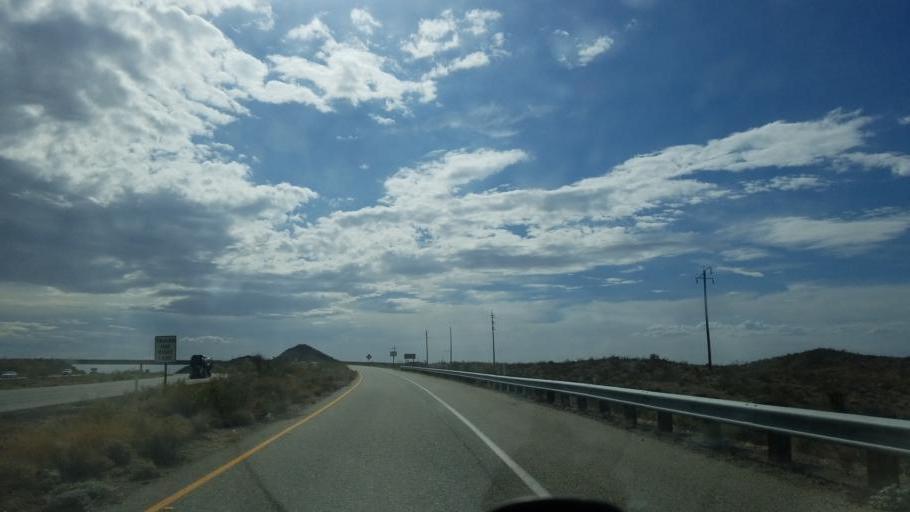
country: US
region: California
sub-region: San Bernardino County
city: Needles
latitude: 34.8310
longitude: -115.0461
